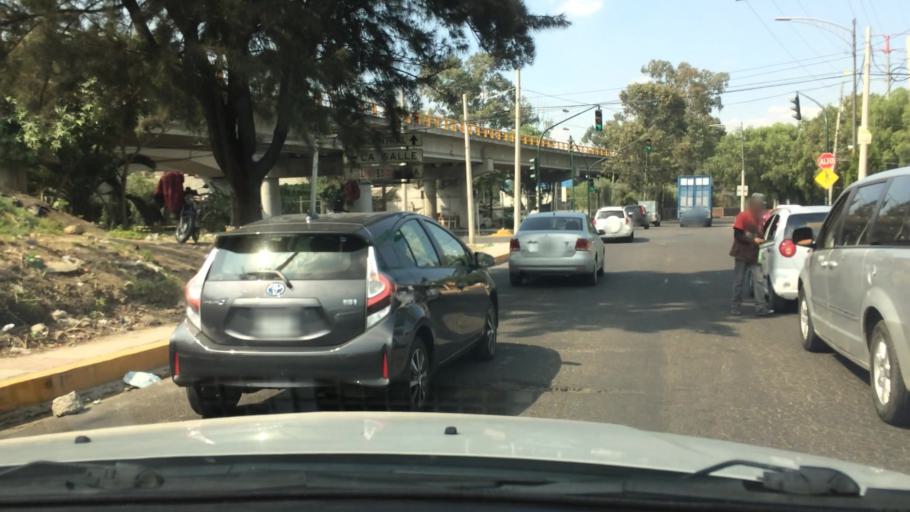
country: MX
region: Mexico
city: Colonia Lindavista
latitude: 19.5186
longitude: -99.1424
